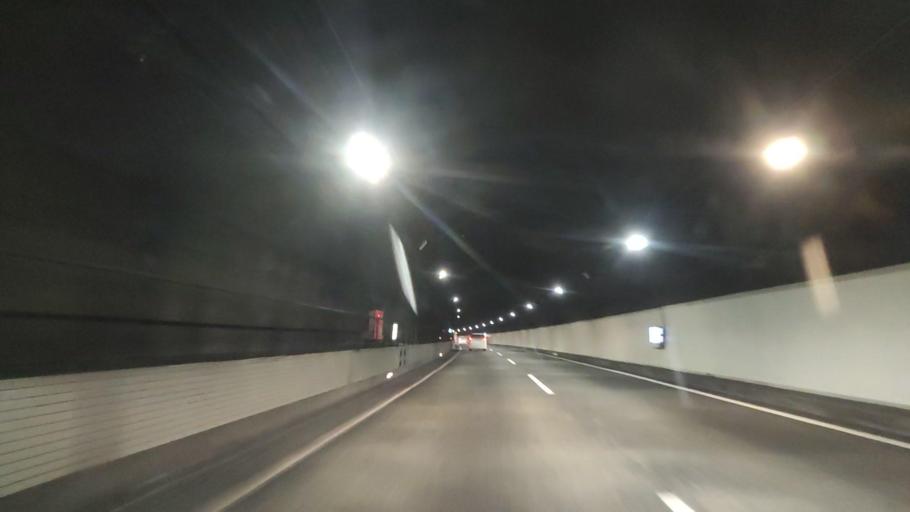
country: JP
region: Okayama
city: Okayama-shi
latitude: 34.6809
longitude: 133.8445
